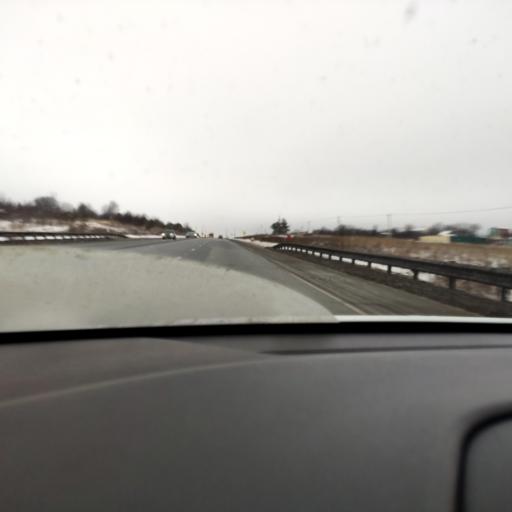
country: RU
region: Tatarstan
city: Verkhniy Uslon
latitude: 55.7217
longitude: 48.8327
